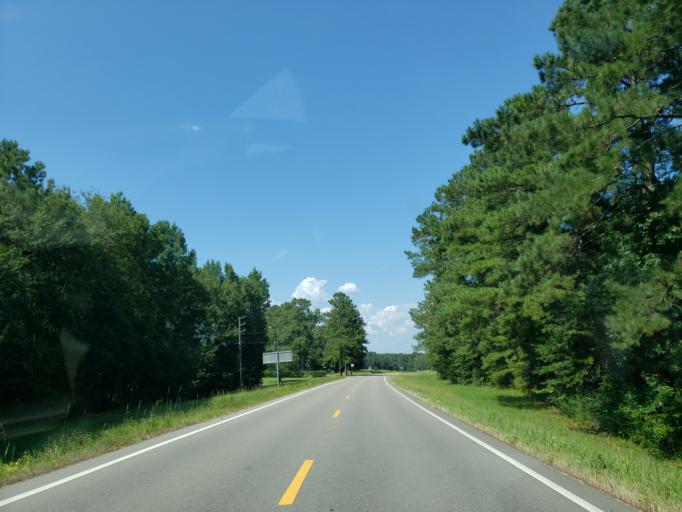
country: US
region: Mississippi
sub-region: Lamar County
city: Sumrall
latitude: 31.4324
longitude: -89.5412
